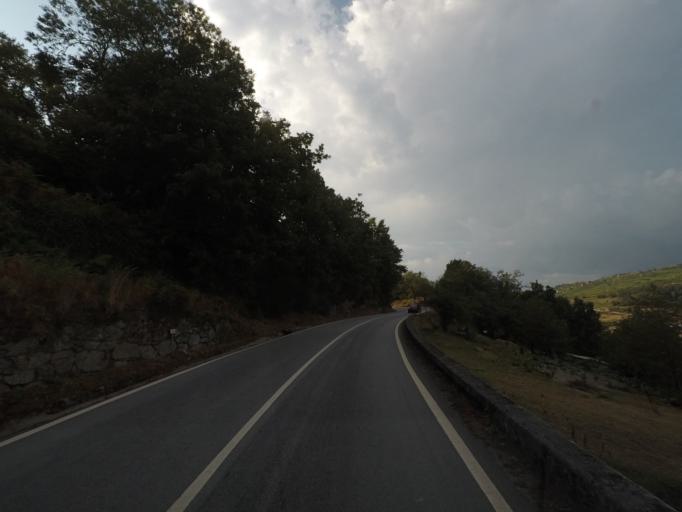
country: PT
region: Porto
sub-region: Baiao
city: Valadares
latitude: 41.1899
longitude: -7.9442
